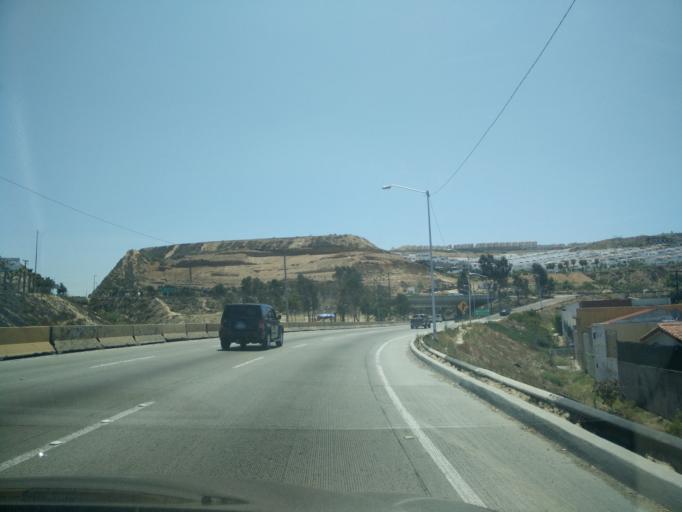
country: US
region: California
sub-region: San Diego County
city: Imperial Beach
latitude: 32.5340
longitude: -117.1107
